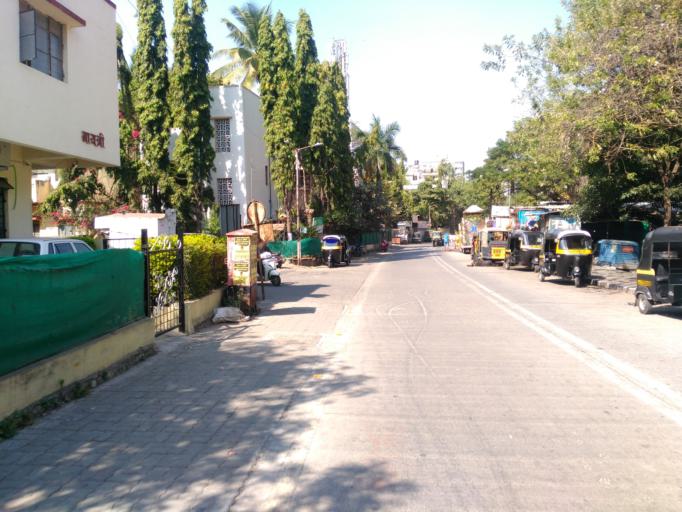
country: IN
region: Maharashtra
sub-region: Pune Division
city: Pune
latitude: 18.4822
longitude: 73.8519
